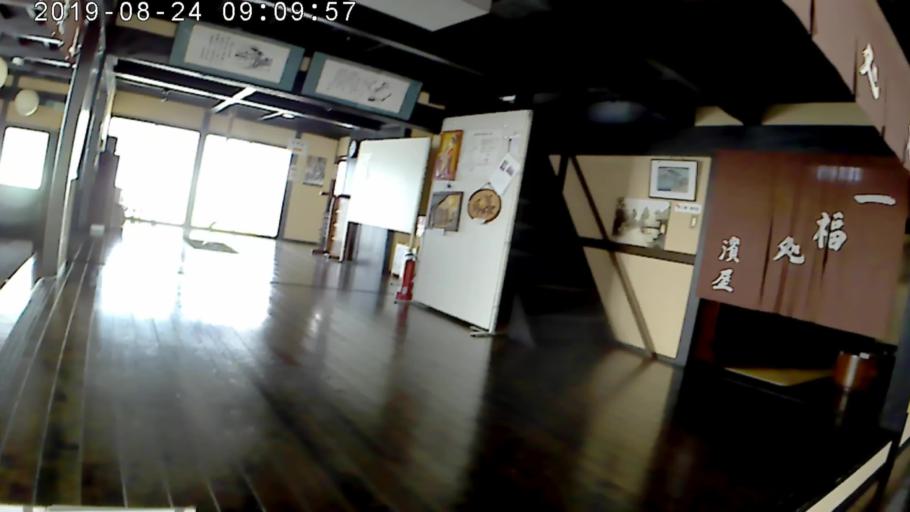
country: JP
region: Nagano
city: Kamimaruko
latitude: 36.2531
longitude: 138.2700
